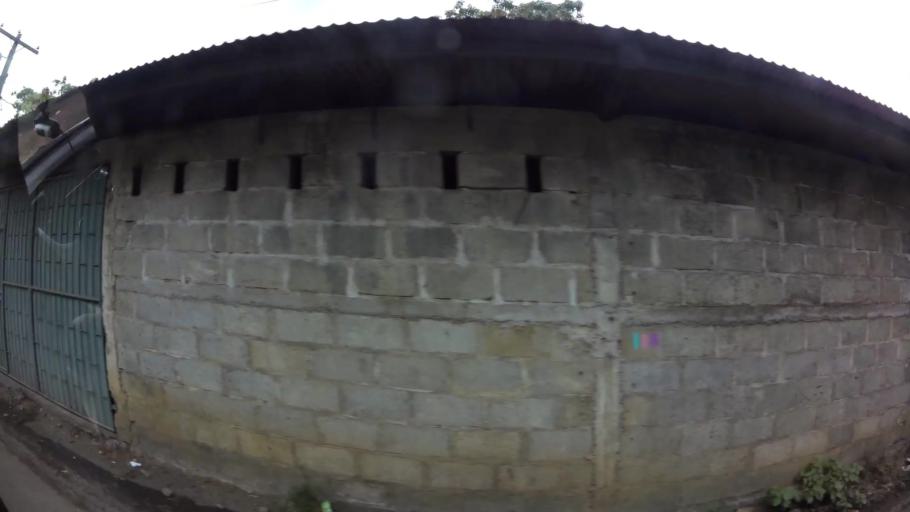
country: NI
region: Leon
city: Leon
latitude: 12.4246
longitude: -86.8874
